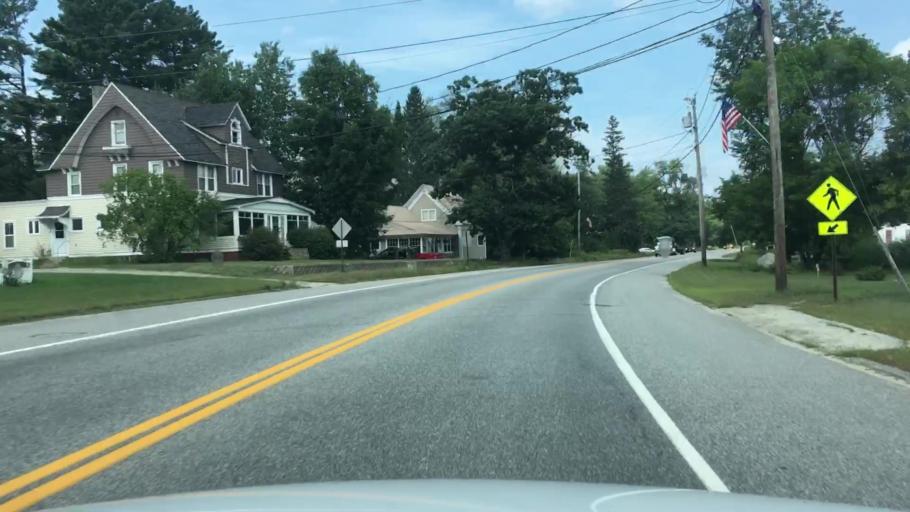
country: US
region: Maine
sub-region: Oxford County
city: Canton
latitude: 44.4419
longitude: -70.3166
